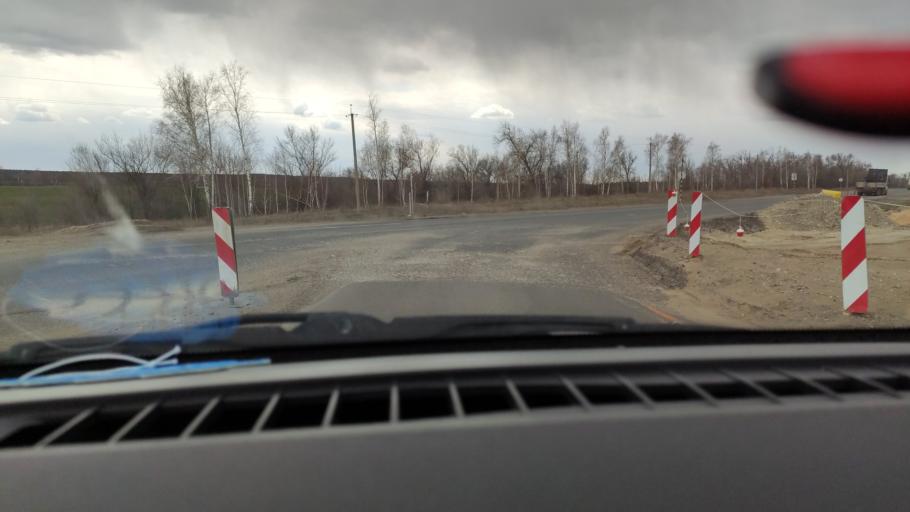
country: RU
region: Saratov
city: Sinodskoye
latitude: 52.0178
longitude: 46.7011
